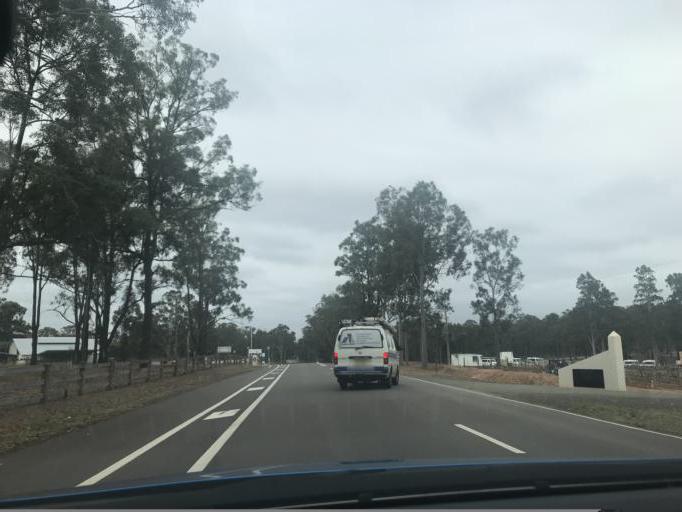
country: AU
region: New South Wales
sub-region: Cessnock
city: Branxton
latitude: -32.7110
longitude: 151.2569
